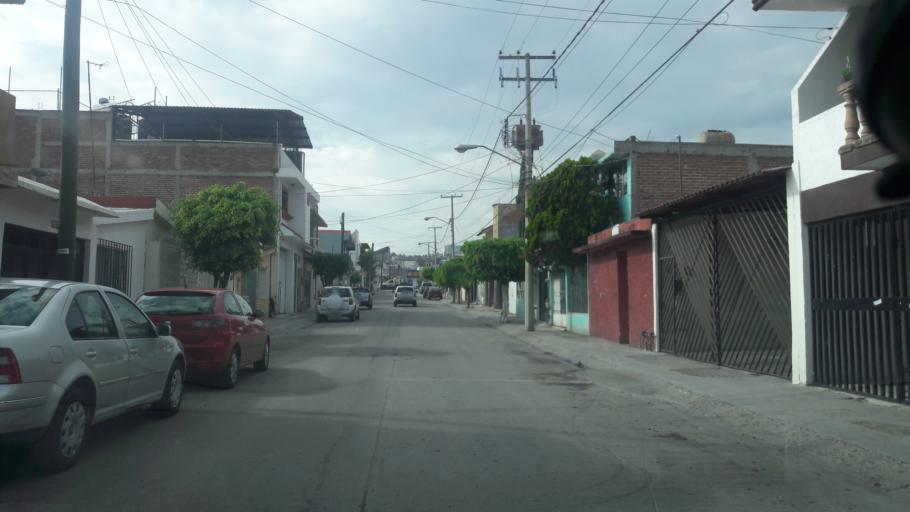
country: MX
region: Guanajuato
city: Leon
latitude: 21.1440
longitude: -101.6997
